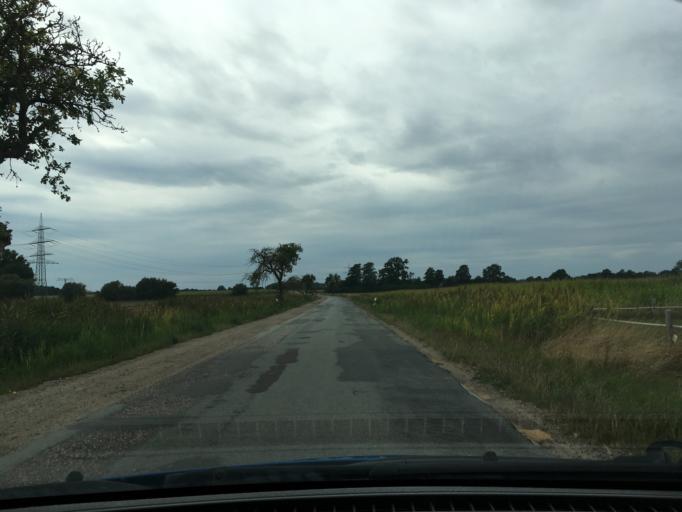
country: DE
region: Mecklenburg-Vorpommern
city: Wittenburg
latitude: 53.5160
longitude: 11.1077
